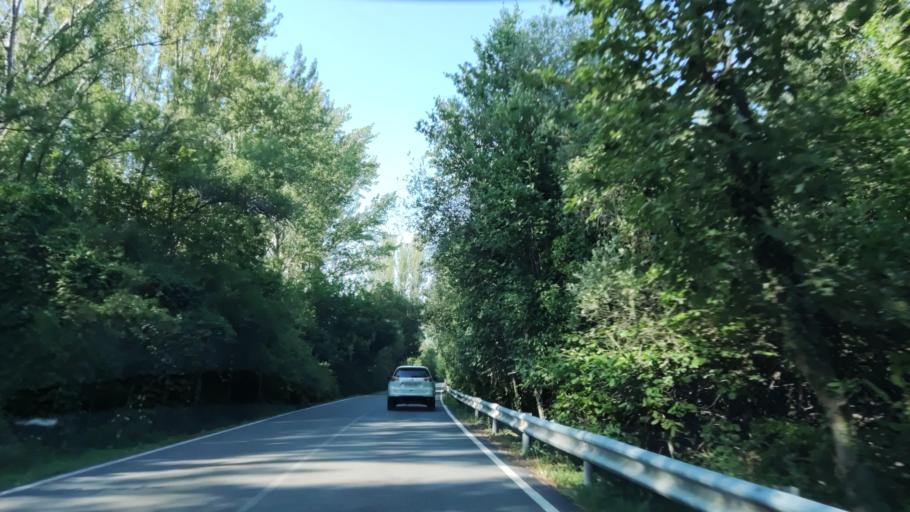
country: ES
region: Madrid
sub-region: Provincia de Madrid
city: Rascafria
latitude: 40.8900
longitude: -3.8852
